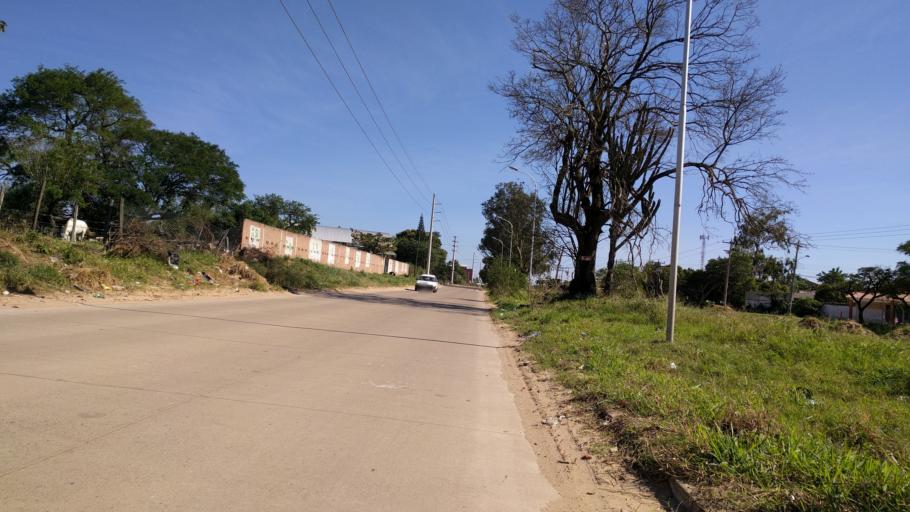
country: BO
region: Santa Cruz
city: Santa Cruz de la Sierra
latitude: -17.8676
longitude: -63.2000
